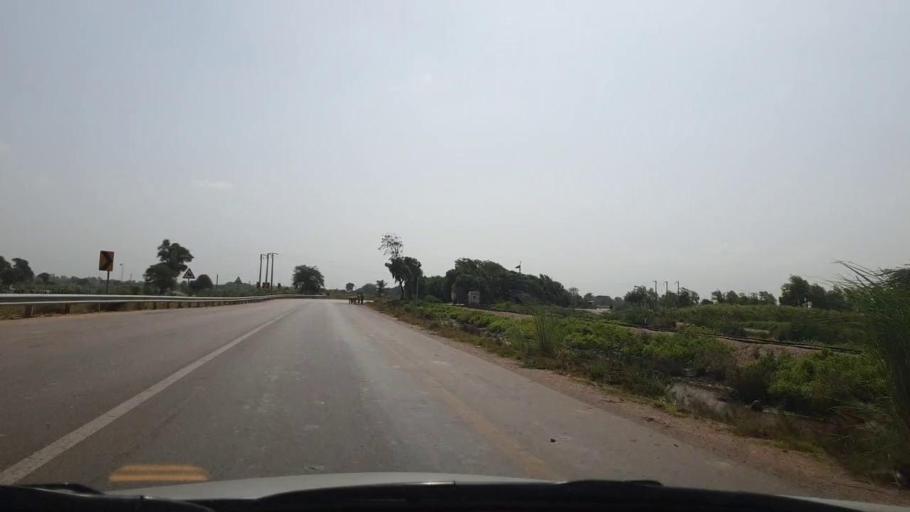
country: PK
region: Sindh
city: Matli
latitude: 25.0424
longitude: 68.6402
